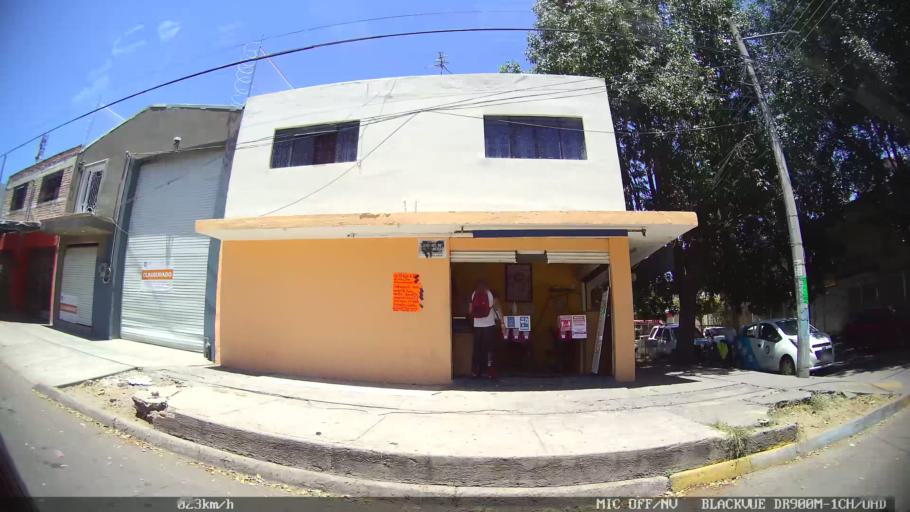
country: MX
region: Jalisco
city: Tlaquepaque
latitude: 20.6649
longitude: -103.2808
